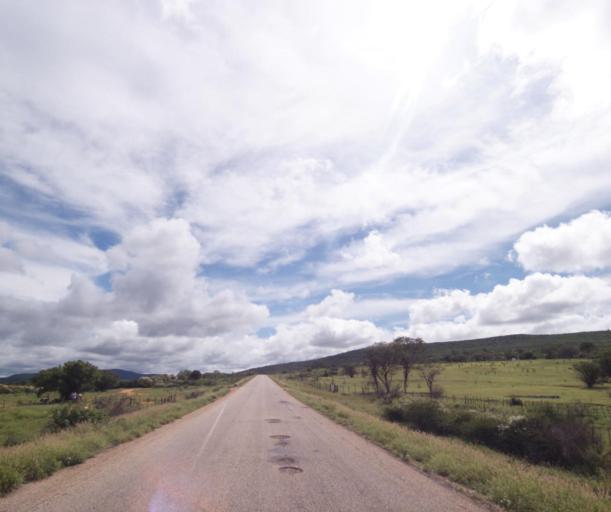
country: BR
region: Bahia
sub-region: Brumado
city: Brumado
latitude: -14.2104
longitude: -41.6301
